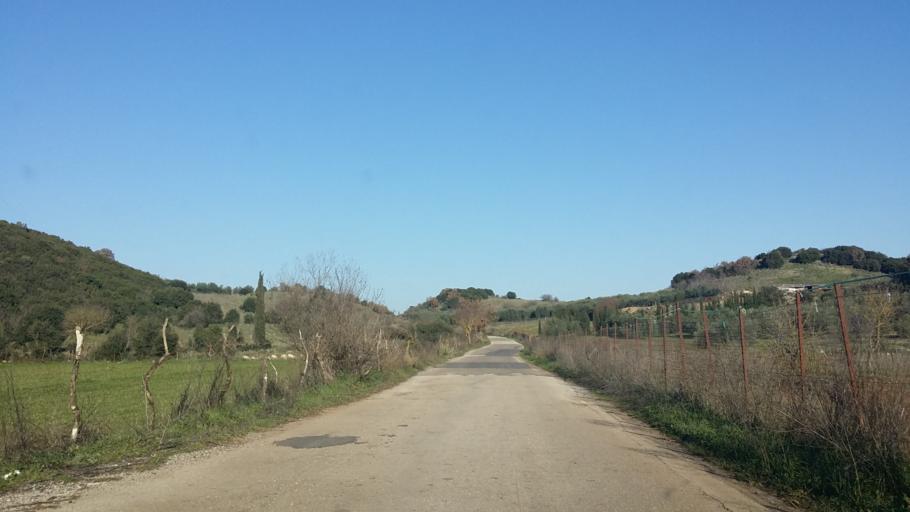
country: GR
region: West Greece
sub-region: Nomos Aitolias kai Akarnanias
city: Katouna
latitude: 38.7906
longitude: 21.1056
